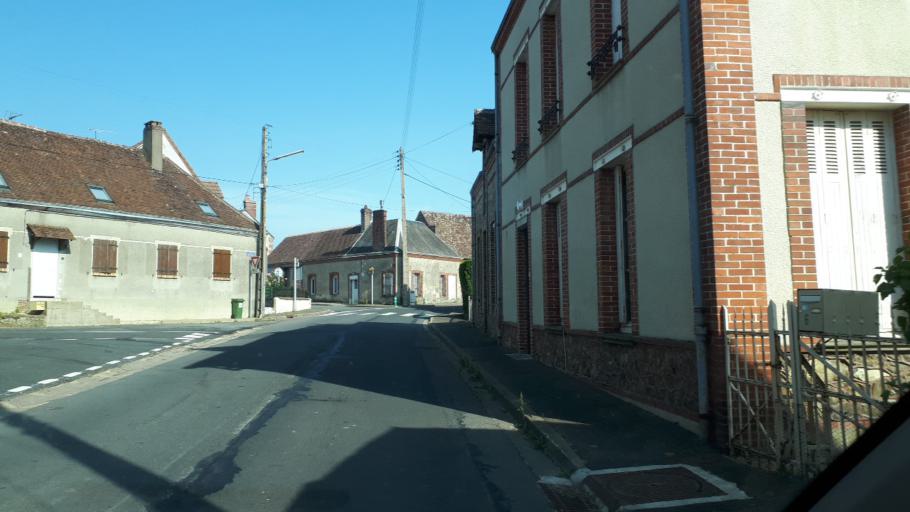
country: FR
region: Centre
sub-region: Departement du Loir-et-Cher
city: La Ville-aux-Clercs
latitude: 47.9583
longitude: 1.0783
